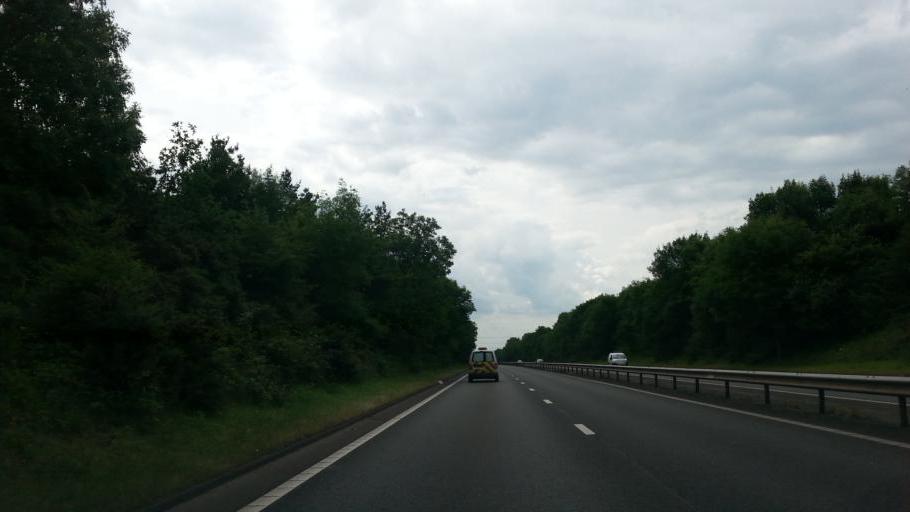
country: GB
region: England
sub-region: Warwickshire
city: Curdworth
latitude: 52.5520
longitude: -1.7748
